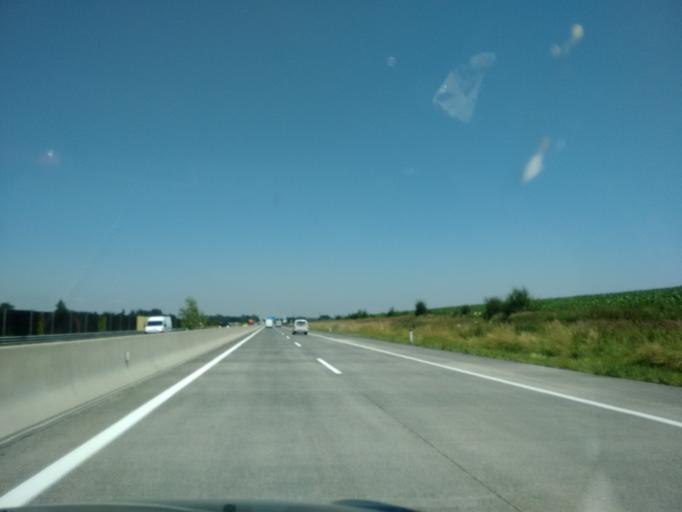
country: AT
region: Upper Austria
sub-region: Politischer Bezirk Gmunden
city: Vorchdorf
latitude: 48.0304
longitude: 13.9751
